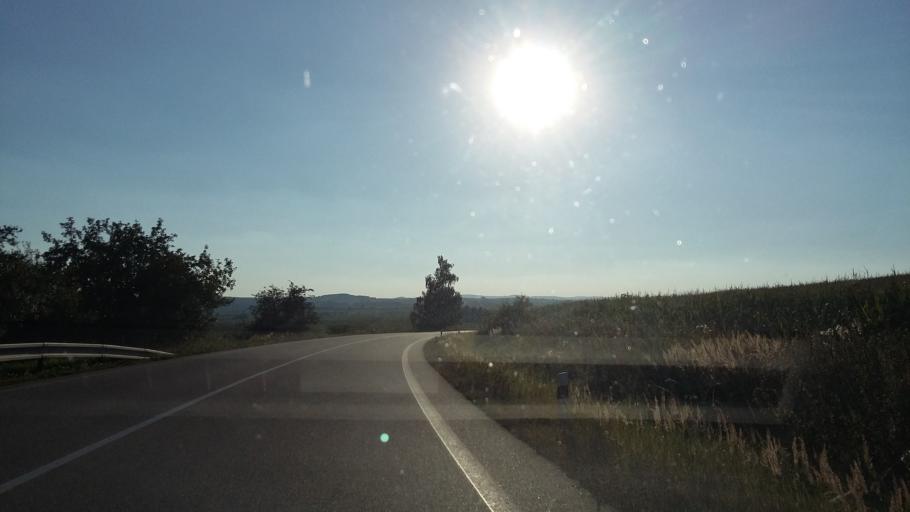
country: CZ
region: Vysocina
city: Luka nad Jihlavou
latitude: 49.3924
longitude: 15.7160
